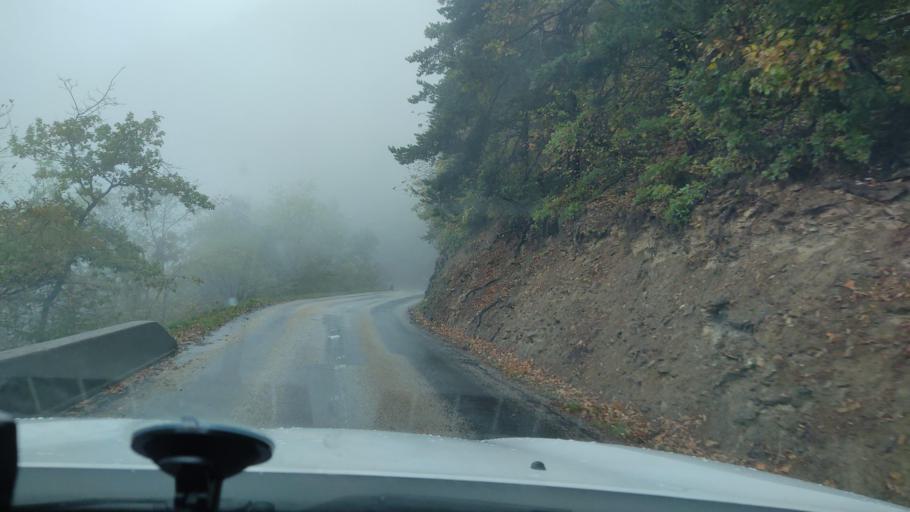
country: FR
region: Rhone-Alpes
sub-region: Departement de la Savoie
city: Les Allues
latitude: 45.4593
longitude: 6.5639
